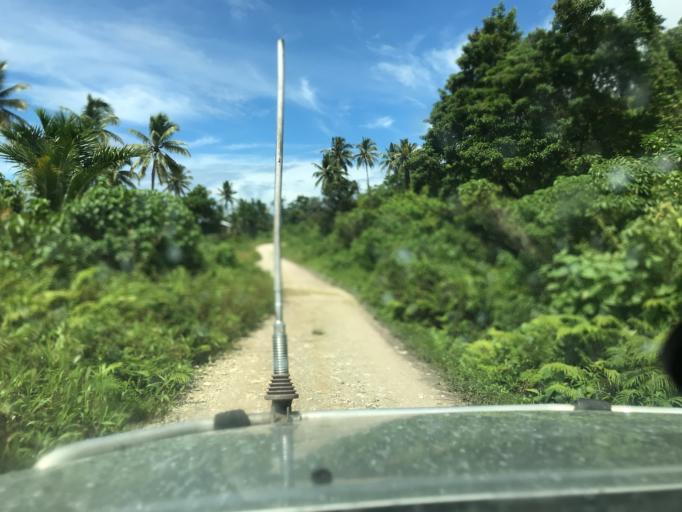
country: SB
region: Malaita
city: Auki
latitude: -8.4547
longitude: 160.8371
